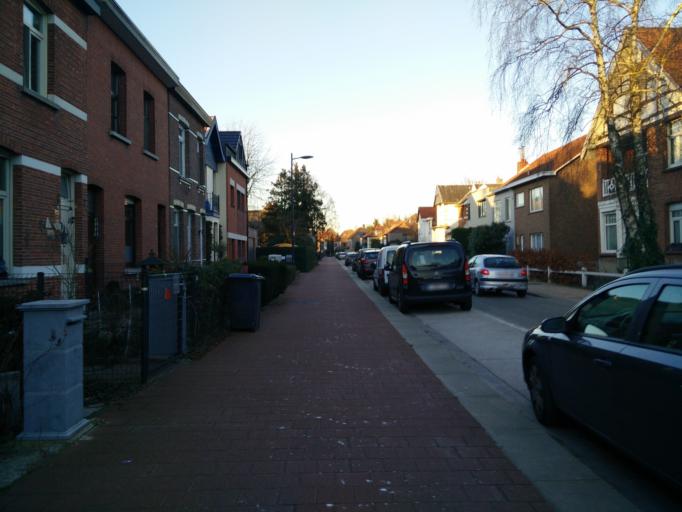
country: BE
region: Flanders
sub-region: Provincie Antwerpen
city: Kapellen
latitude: 51.3167
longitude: 4.4355
